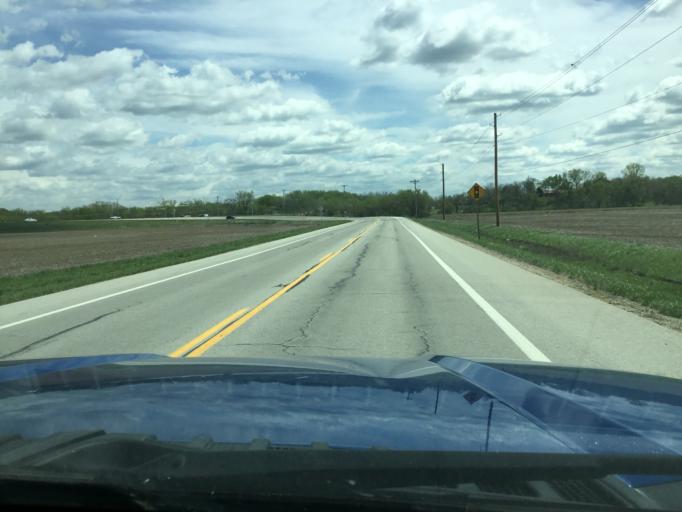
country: US
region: Kansas
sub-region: Douglas County
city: Lawrence
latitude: 38.9104
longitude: -95.2641
